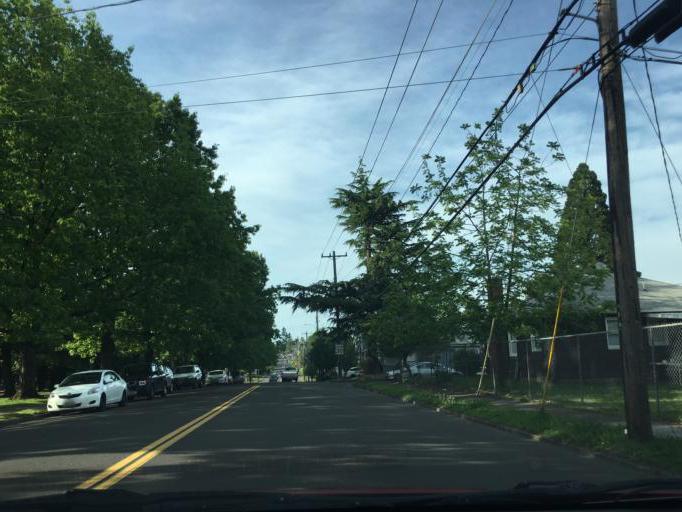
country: US
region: Oregon
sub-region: Multnomah County
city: Lents
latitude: 45.5141
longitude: -122.5691
